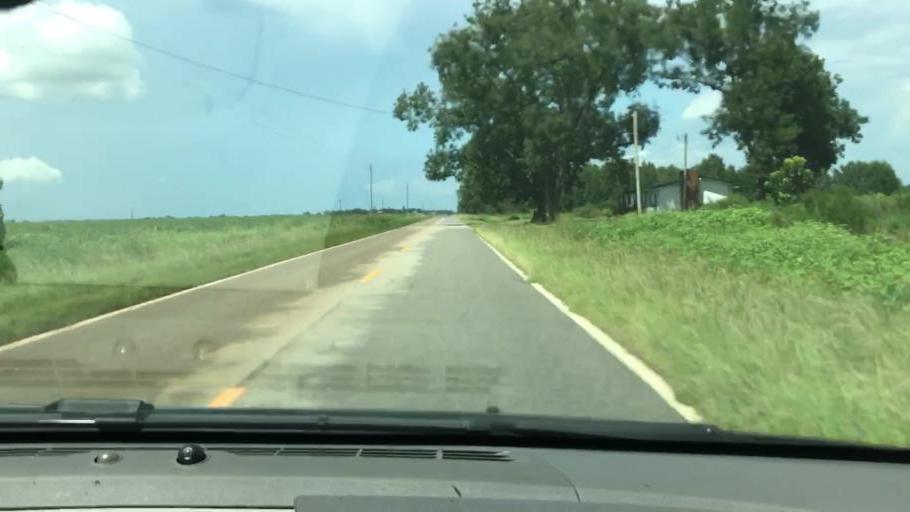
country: US
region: Georgia
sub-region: Seminole County
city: Donalsonville
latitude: 31.0950
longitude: -84.9962
